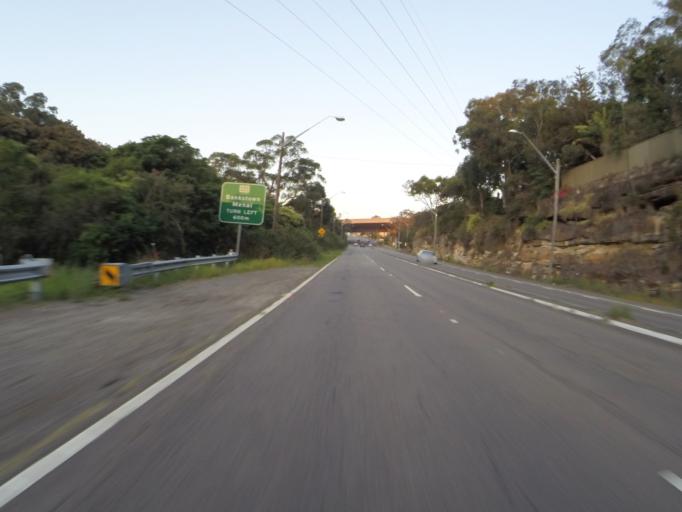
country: AU
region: New South Wales
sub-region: Bankstown
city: Padstow
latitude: -33.9692
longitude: 151.0289
